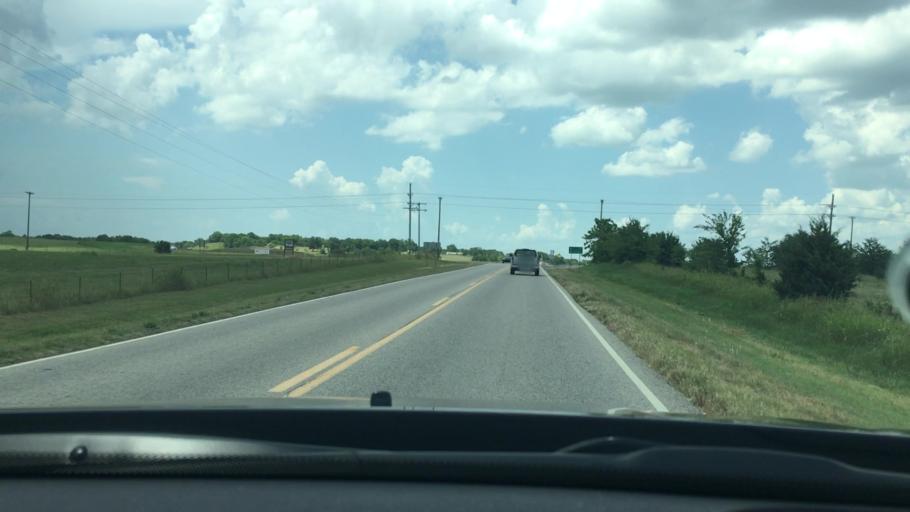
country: US
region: Oklahoma
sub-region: Pontotoc County
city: Ada
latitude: 34.7221
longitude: -96.6348
